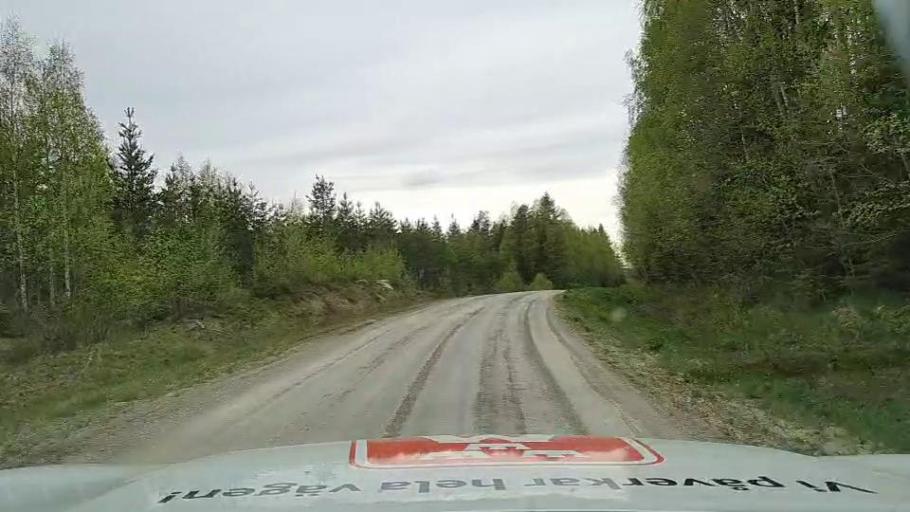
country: SE
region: Jaemtland
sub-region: Bergs Kommun
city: Hoverberg
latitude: 62.6772
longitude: 14.7626
